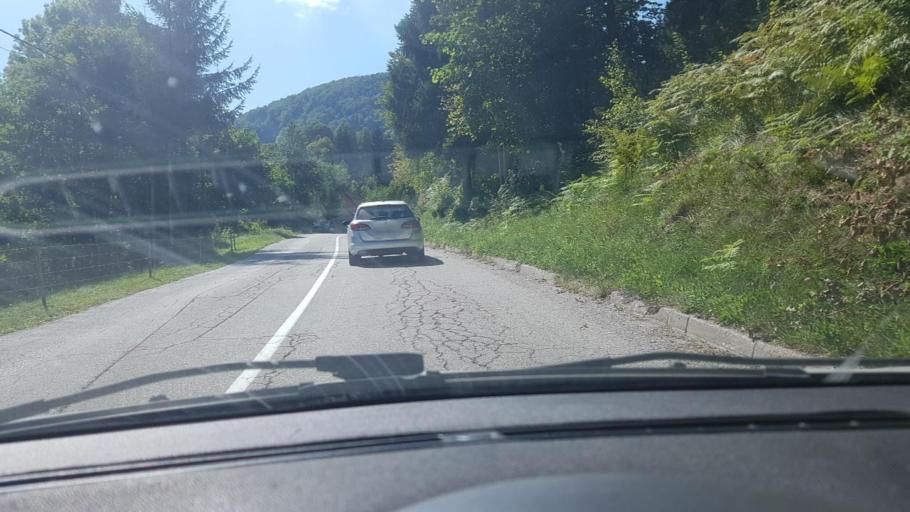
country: HR
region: Primorsko-Goranska
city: Vrbovsko
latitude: 45.3792
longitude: 14.9761
